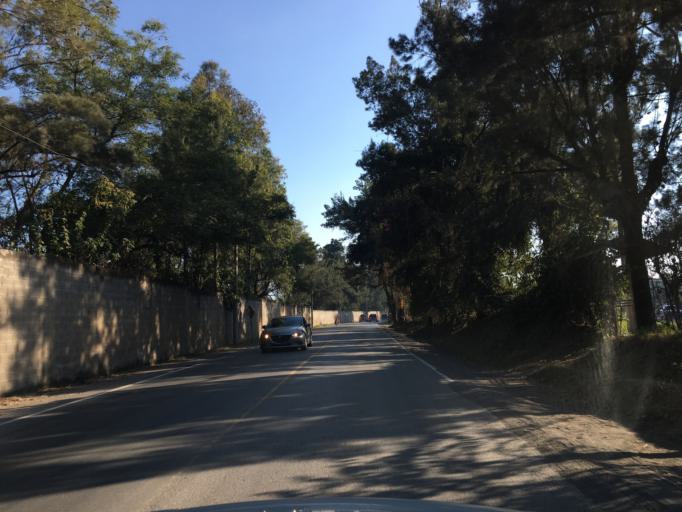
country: GT
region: Guatemala
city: Villa Nueva
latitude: 14.5331
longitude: -90.6166
